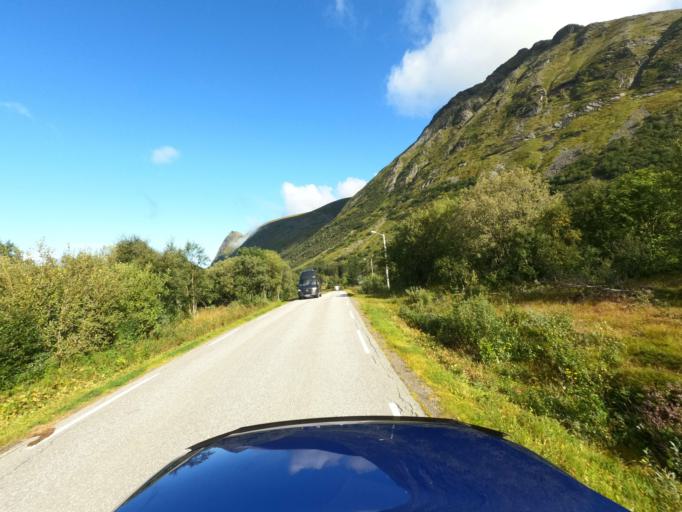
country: NO
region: Nordland
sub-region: Vagan
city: Kabelvag
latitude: 68.2910
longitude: 14.3251
